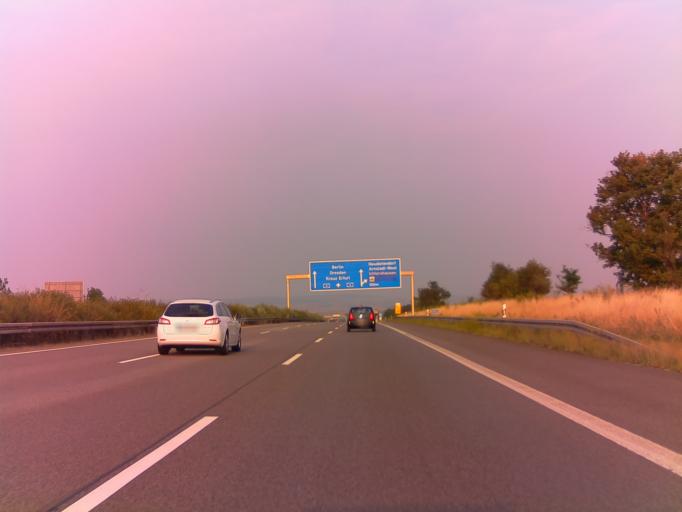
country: DE
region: Thuringia
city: Neudietendorf
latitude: 50.8937
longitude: 10.9168
